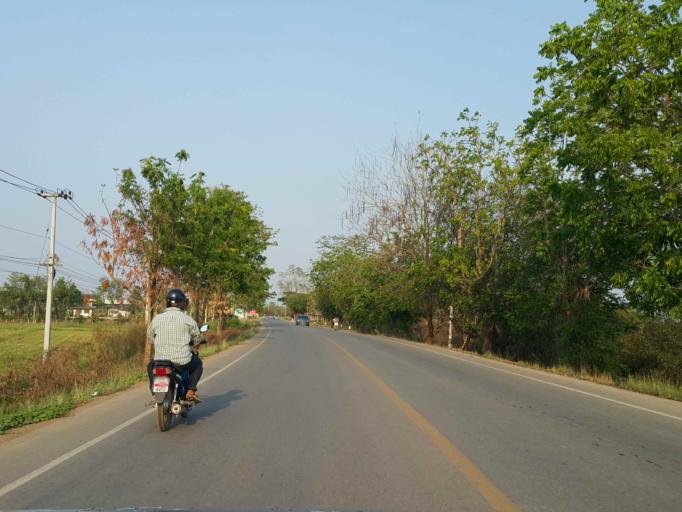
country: TH
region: Sukhothai
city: Sawankhalok
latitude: 17.3097
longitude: 99.8091
